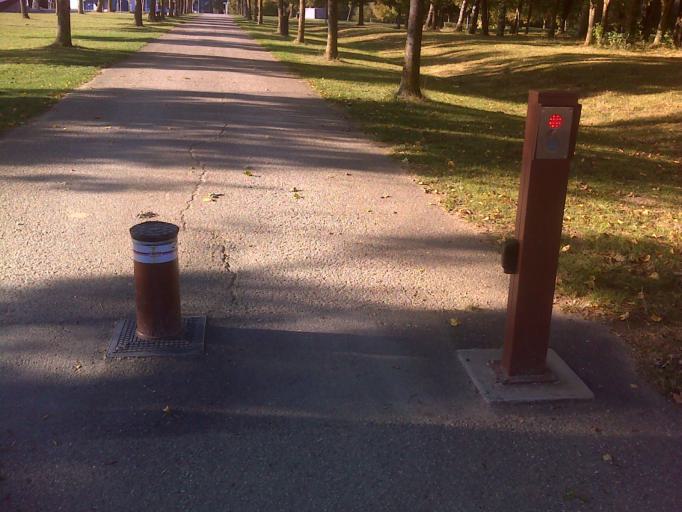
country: FR
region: Lorraine
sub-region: Departement de la Meuse
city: Vigneulles-les-Hattonchatel
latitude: 48.9267
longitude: 5.7569
